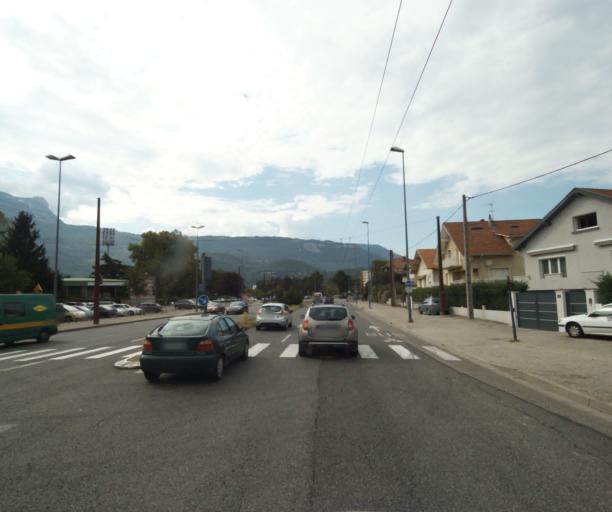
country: FR
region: Rhone-Alpes
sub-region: Departement de l'Isere
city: Grenoble
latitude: 45.1669
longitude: 5.7062
